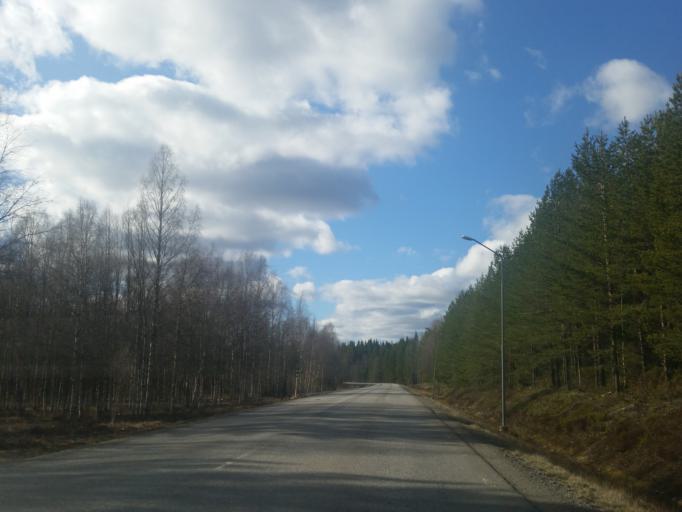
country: SE
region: Vaesterbotten
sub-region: Robertsfors Kommun
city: Robertsfors
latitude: 64.1992
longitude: 20.8339
